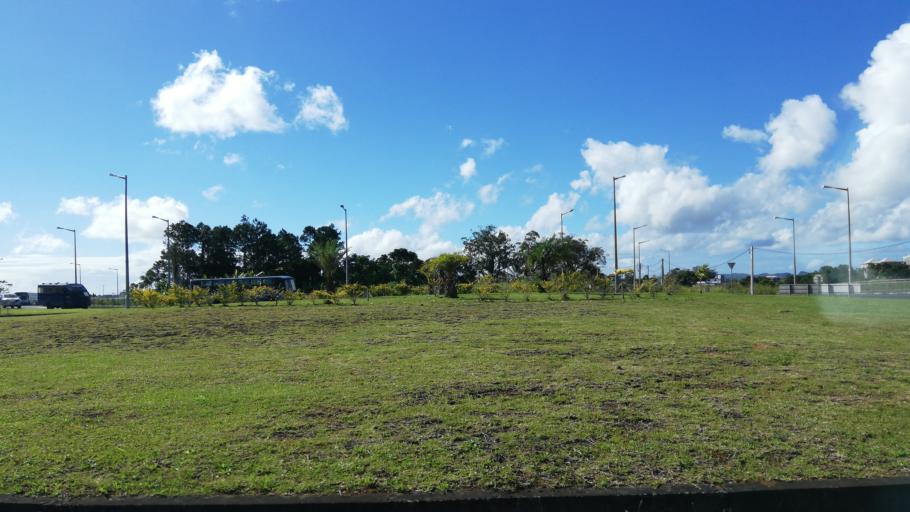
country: MU
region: Moka
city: Providence
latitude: -20.2462
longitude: 57.6046
